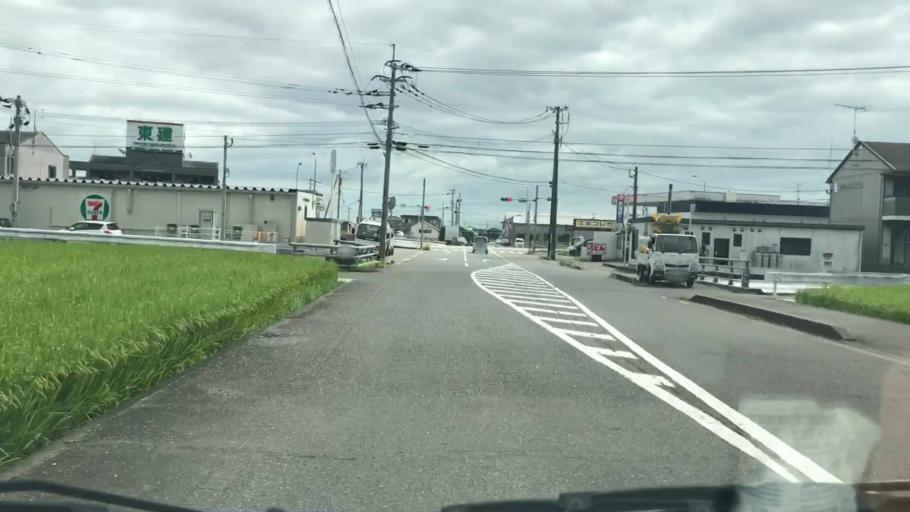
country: JP
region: Saga Prefecture
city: Saga-shi
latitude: 33.2198
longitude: 130.1693
